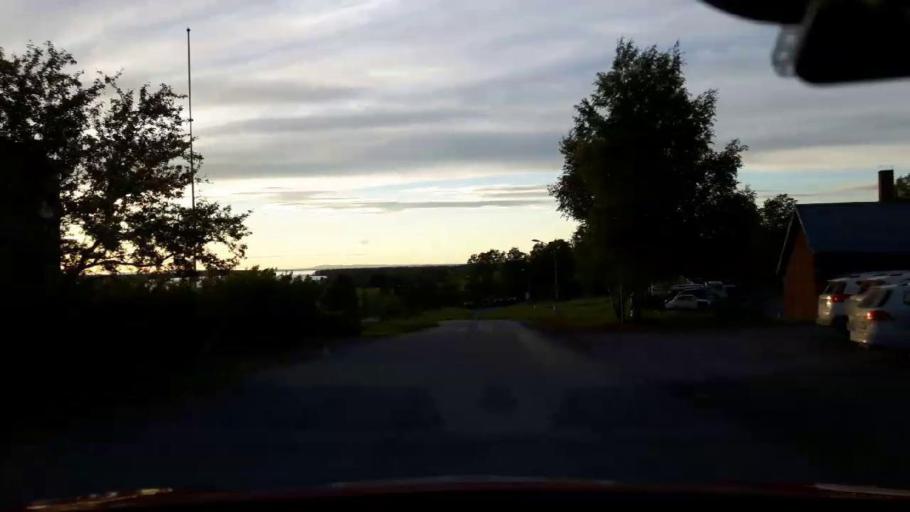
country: SE
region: Jaemtland
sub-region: OEstersunds Kommun
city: Ostersund
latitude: 63.1062
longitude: 14.4364
